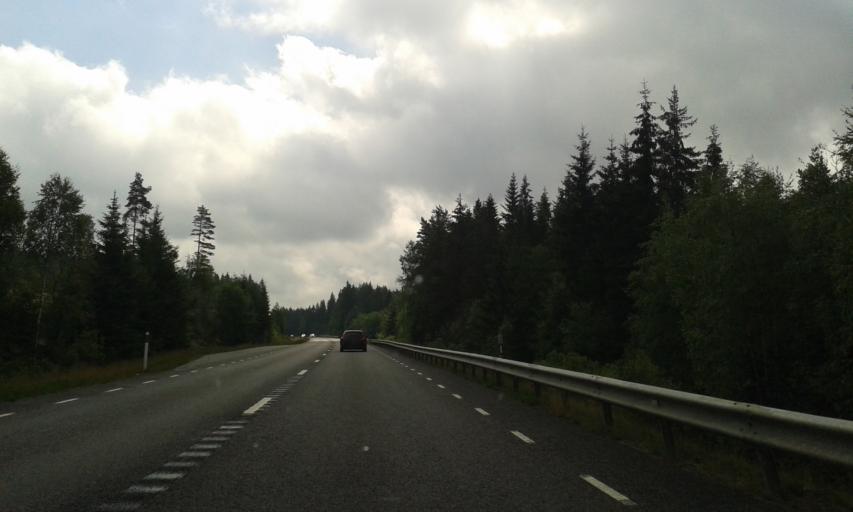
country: SE
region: Vaestra Goetaland
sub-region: Tranemo Kommun
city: Tranemo
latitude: 57.4446
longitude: 13.4215
